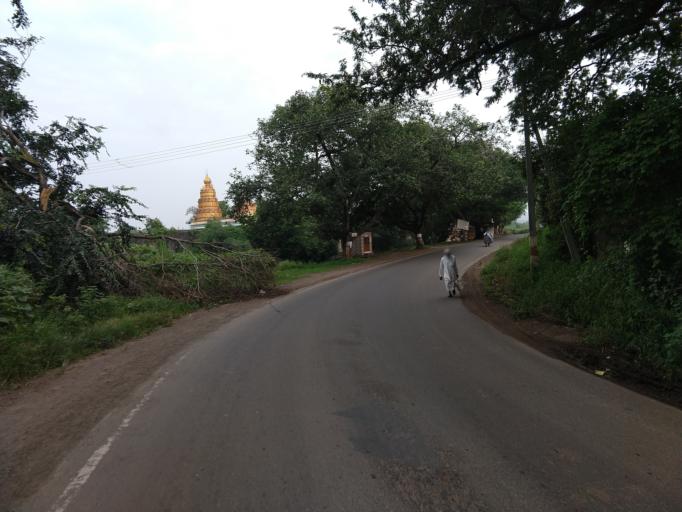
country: IN
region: Maharashtra
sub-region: Pune Division
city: Sasvad
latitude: 18.3589
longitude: 73.9961
